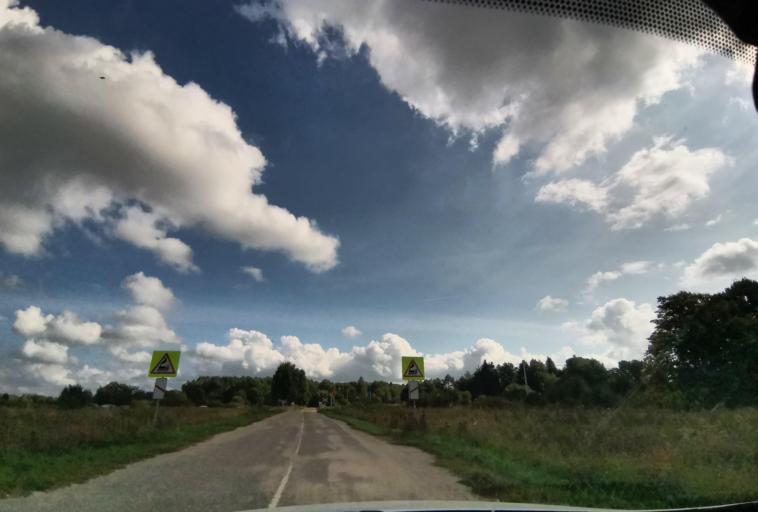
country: PL
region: Warmian-Masurian Voivodeship
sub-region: Powiat goldapski
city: Goldap
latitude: 54.4189
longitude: 22.3991
